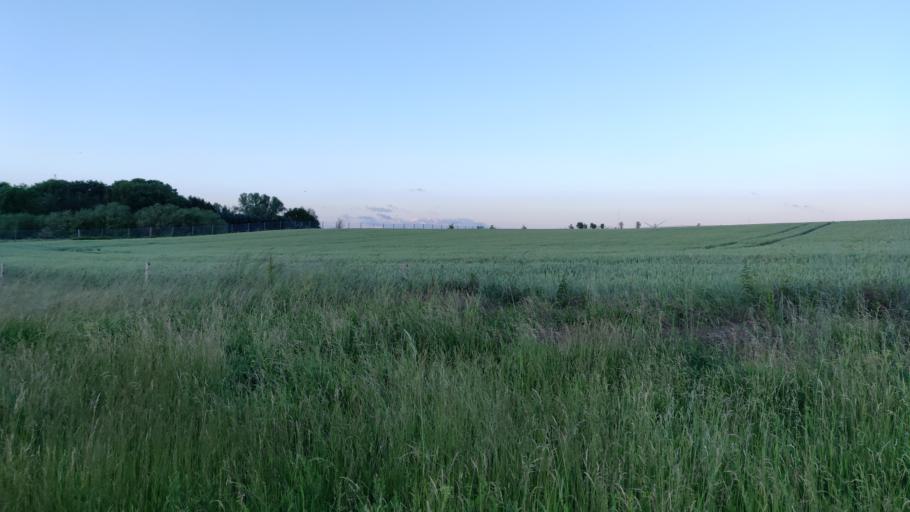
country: DK
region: Zealand
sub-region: Roskilde Kommune
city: Roskilde
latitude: 55.6836
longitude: 12.0768
